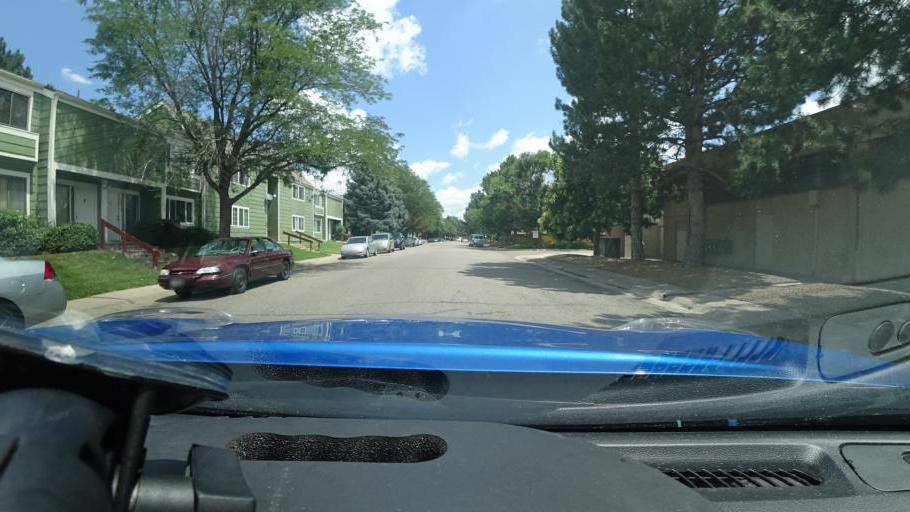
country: US
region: Colorado
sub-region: Adams County
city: Aurora
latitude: 39.6999
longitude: -104.8466
